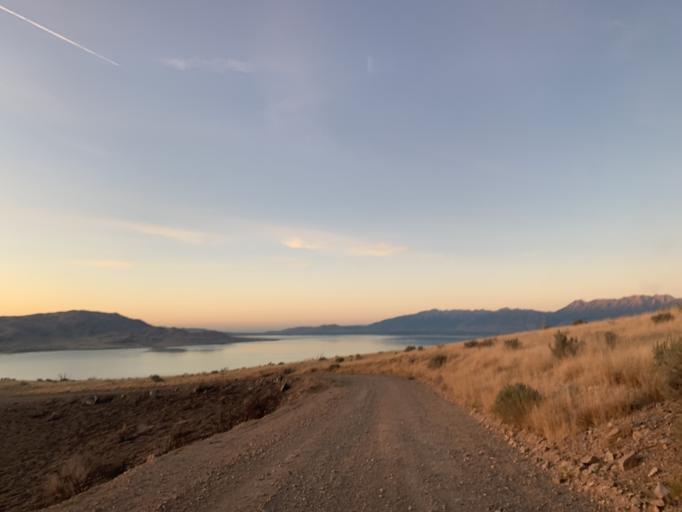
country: US
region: Utah
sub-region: Utah County
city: West Mountain
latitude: 40.1148
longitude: -111.8232
